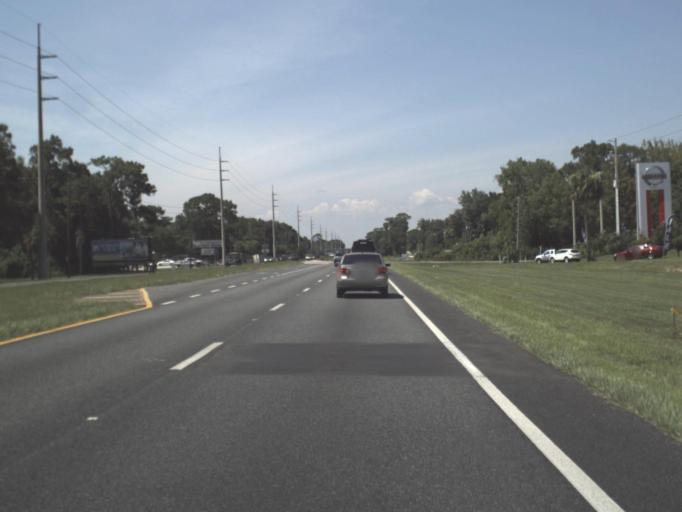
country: US
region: Florida
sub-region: Citrus County
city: Homosassa Springs
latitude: 28.8479
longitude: -82.5794
